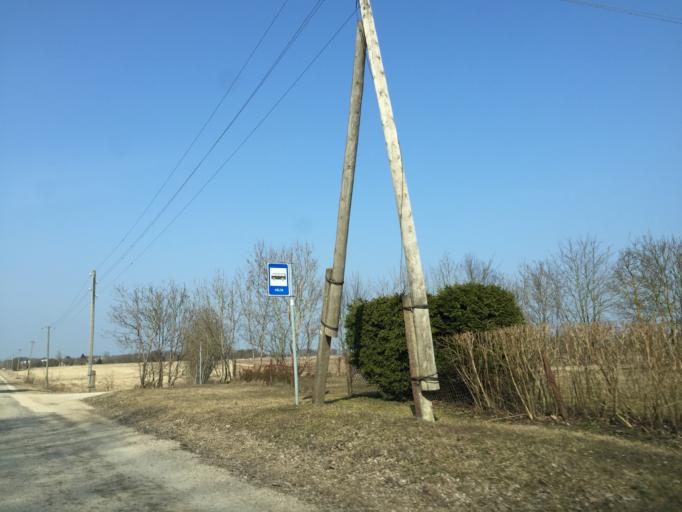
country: EE
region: Saare
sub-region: Orissaare vald
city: Orissaare
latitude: 58.4904
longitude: 23.1177
